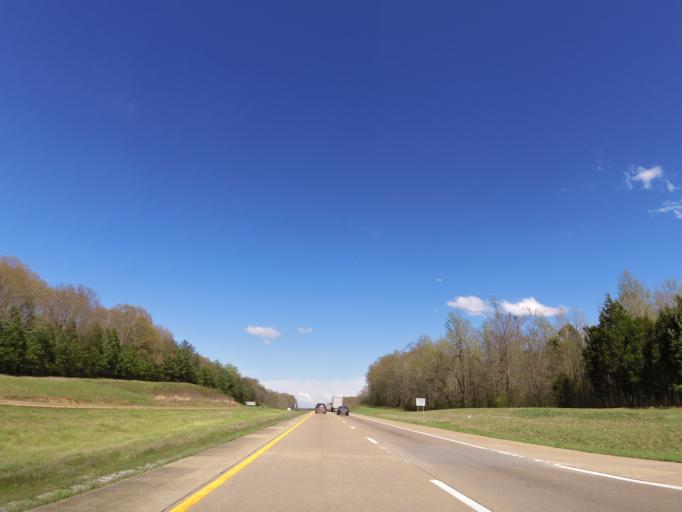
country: US
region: Tennessee
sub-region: Gibson County
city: Medina
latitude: 35.7243
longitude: -88.6138
